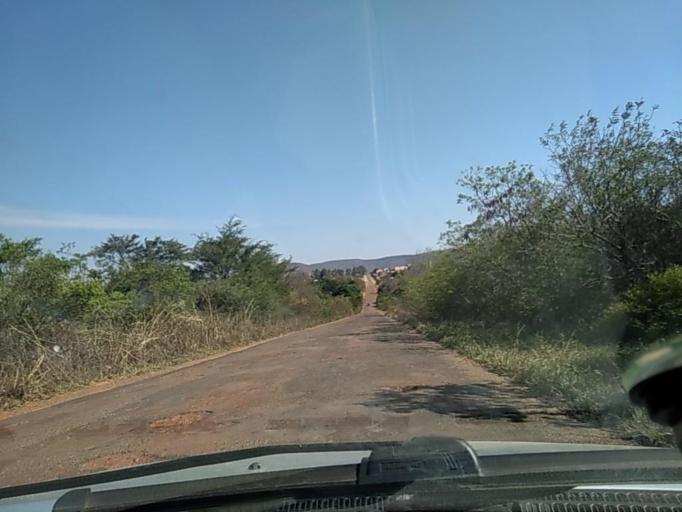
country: BR
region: Bahia
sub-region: Caetite
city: Caetite
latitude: -14.0424
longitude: -42.4860
